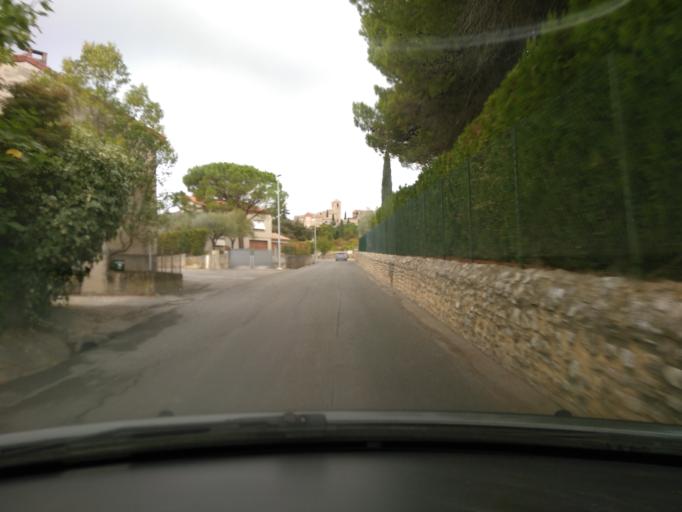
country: FR
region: Rhone-Alpes
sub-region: Departement de la Drome
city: Vinsobres
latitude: 44.3327
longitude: 5.0638
